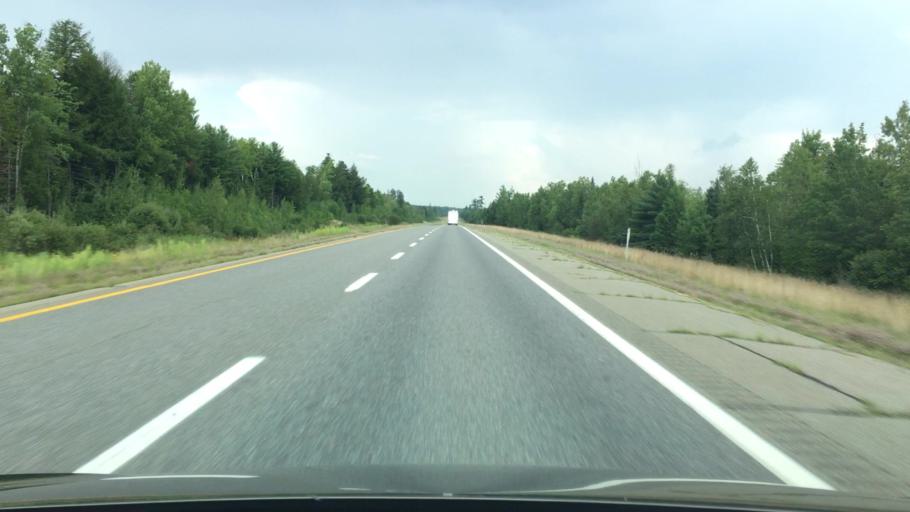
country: US
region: Maine
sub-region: Penobscot County
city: Medway
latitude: 45.5213
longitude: -68.5523
